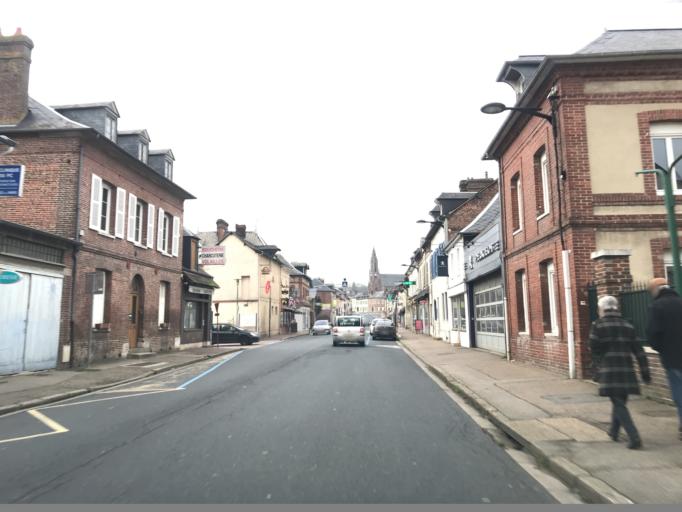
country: FR
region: Haute-Normandie
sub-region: Departement de l'Eure
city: Fleury-sur-Andelle
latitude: 49.3604
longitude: 1.3572
